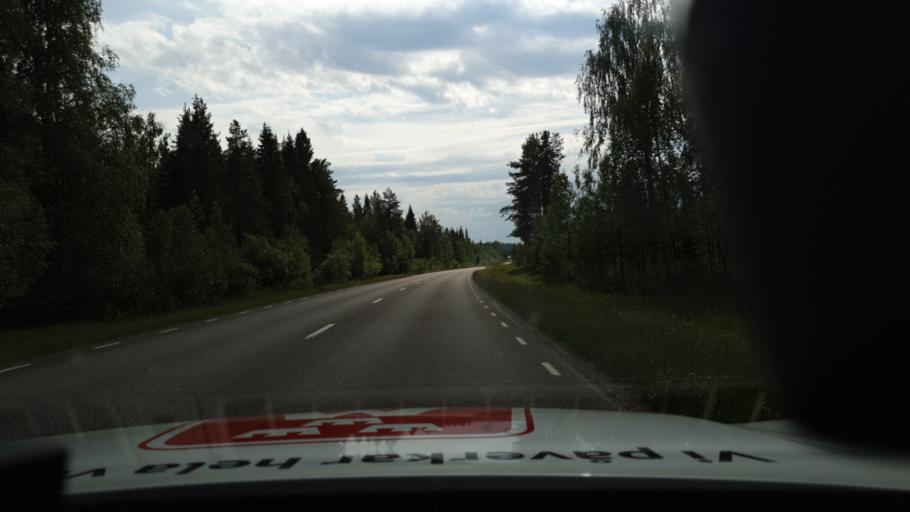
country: SE
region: Norrbotten
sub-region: Lulea Kommun
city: Ranea
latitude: 65.8479
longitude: 22.2718
